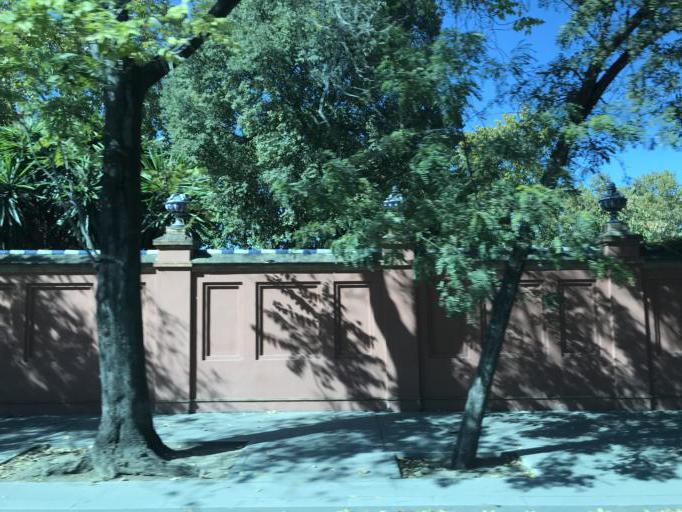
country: ES
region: Andalusia
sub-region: Provincia de Sevilla
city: Sevilla
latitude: 37.3781
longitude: -5.9926
